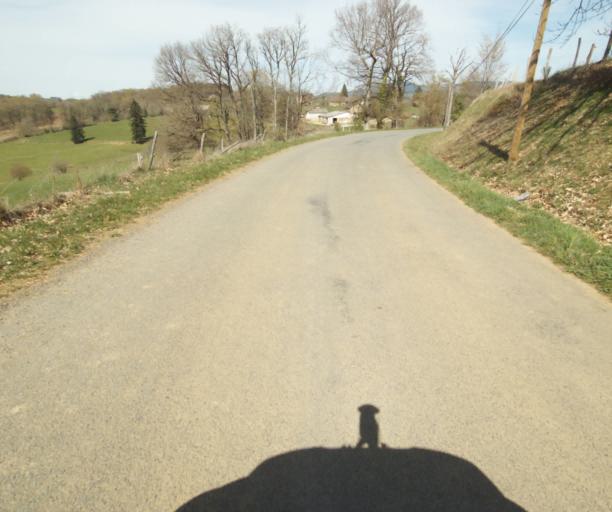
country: FR
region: Limousin
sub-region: Departement de la Correze
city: Seilhac
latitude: 45.3976
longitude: 1.7848
